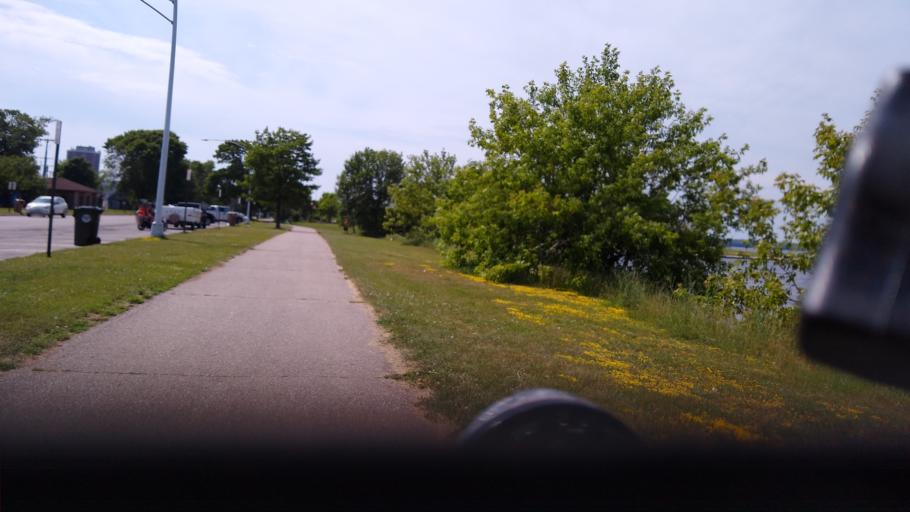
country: US
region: Michigan
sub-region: Delta County
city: Escanaba
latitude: 45.7452
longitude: -87.0452
